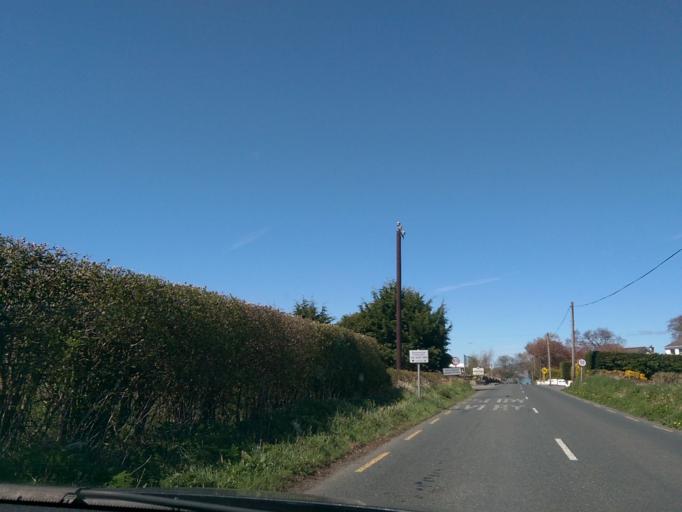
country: IE
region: Leinster
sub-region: Wicklow
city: Carnew
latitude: 52.8592
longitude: -6.5518
